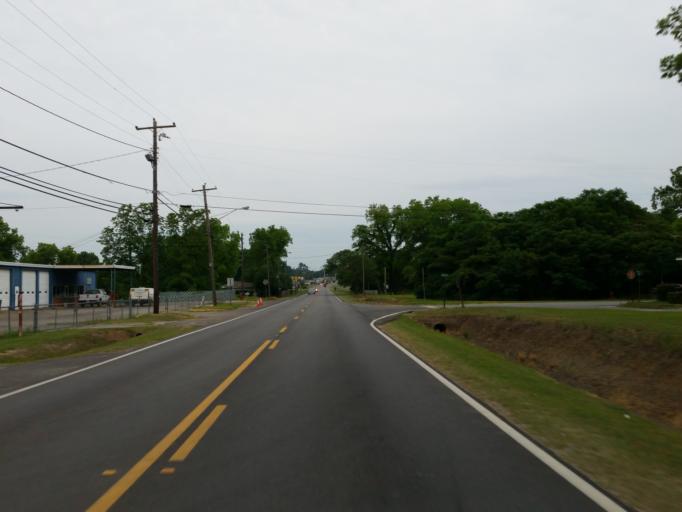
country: US
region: Georgia
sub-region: Dooly County
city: Unadilla
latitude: 32.2565
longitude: -83.7387
